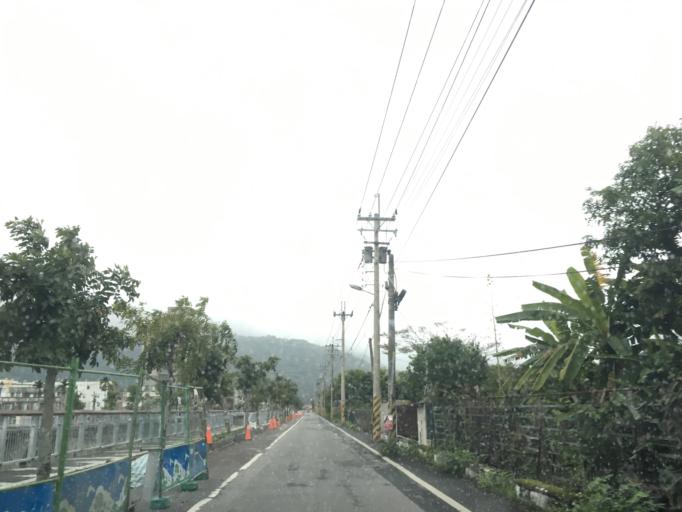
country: TW
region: Taiwan
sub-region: Hualien
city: Hualian
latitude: 23.9834
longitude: 121.5696
